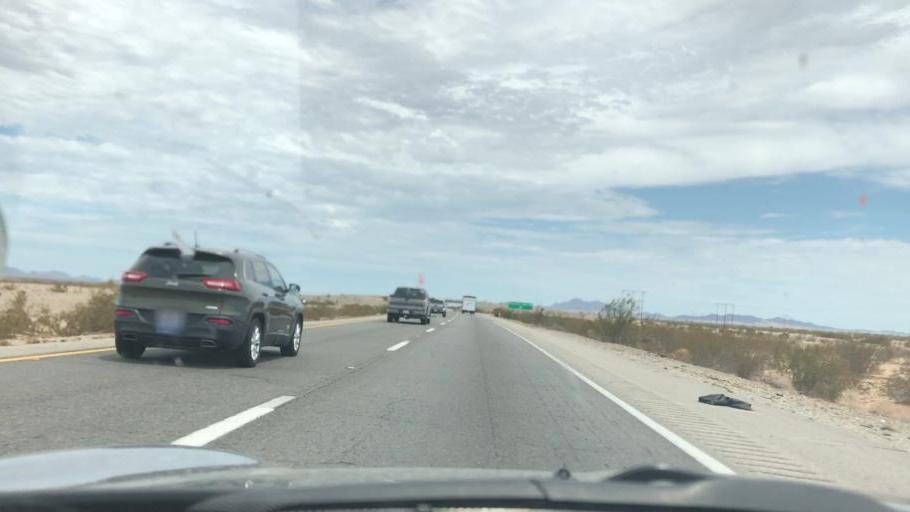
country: US
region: California
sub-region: Riverside County
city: Mesa Verde
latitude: 33.6089
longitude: -114.9960
